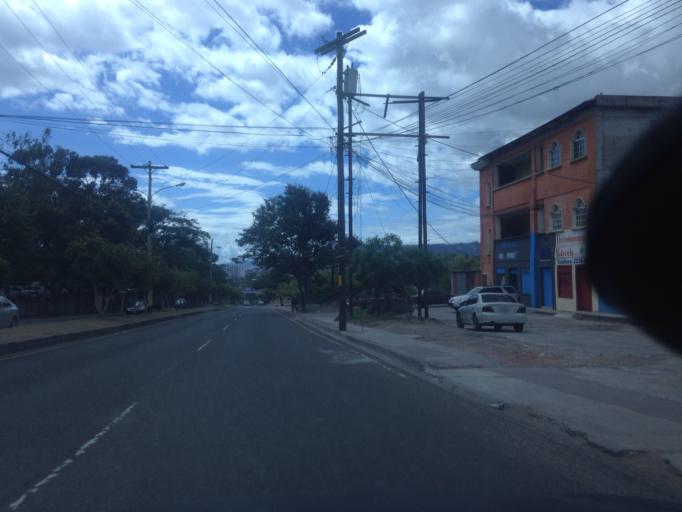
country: HN
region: Francisco Morazan
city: El Tablon
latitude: 14.0667
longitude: -87.1729
